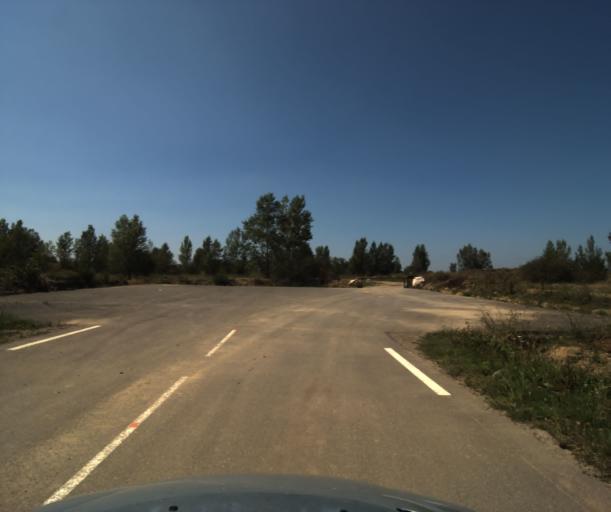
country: FR
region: Midi-Pyrenees
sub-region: Departement de la Haute-Garonne
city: Labastidette
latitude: 43.4522
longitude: 1.2695
